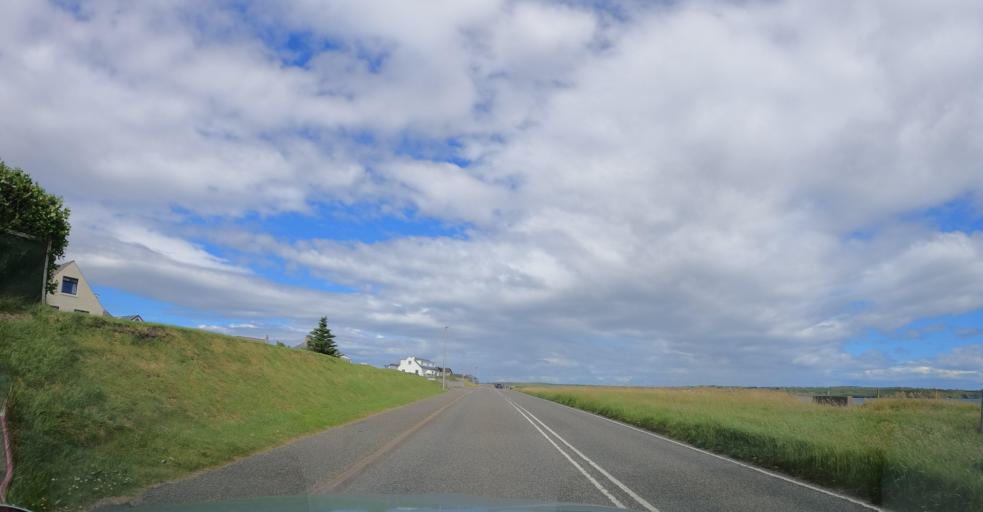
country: GB
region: Scotland
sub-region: Eilean Siar
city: Stornoway
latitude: 58.2050
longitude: -6.3107
